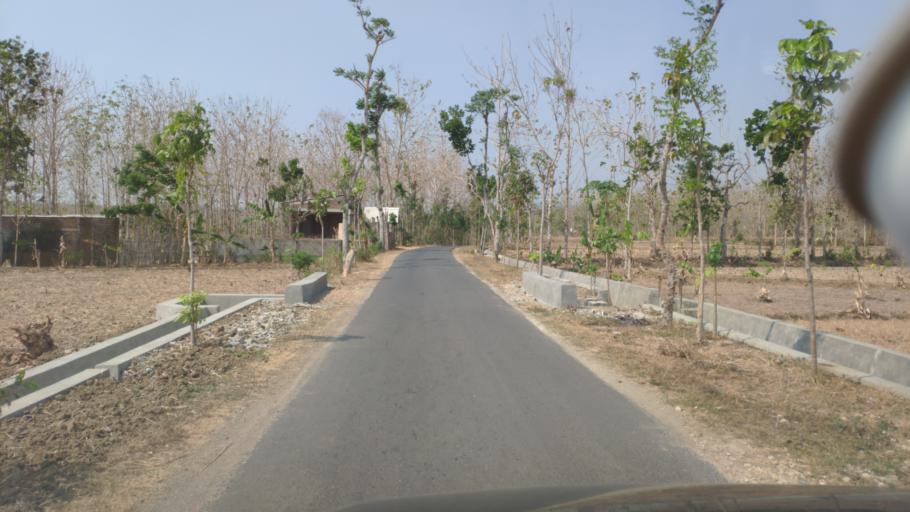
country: ID
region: Central Java
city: Karanggeneng
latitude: -6.9181
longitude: 111.4529
